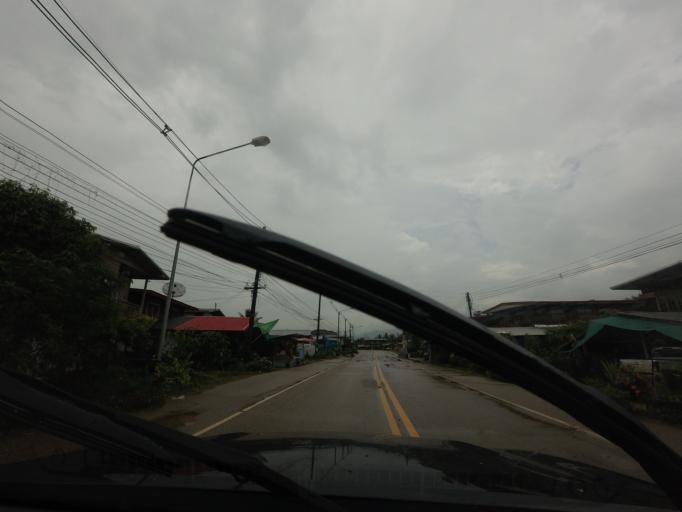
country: TH
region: Nong Khai
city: Sangkhom
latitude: 18.2107
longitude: 102.0750
